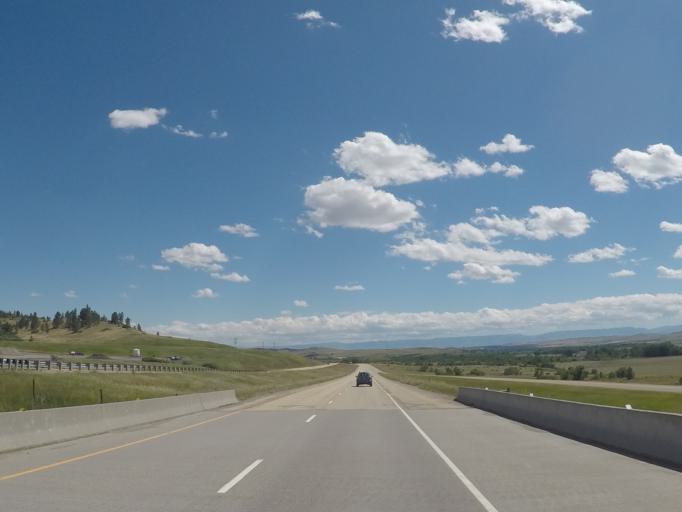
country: US
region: Montana
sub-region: Big Horn County
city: Crow Agency
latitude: 45.3149
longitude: -107.3445
